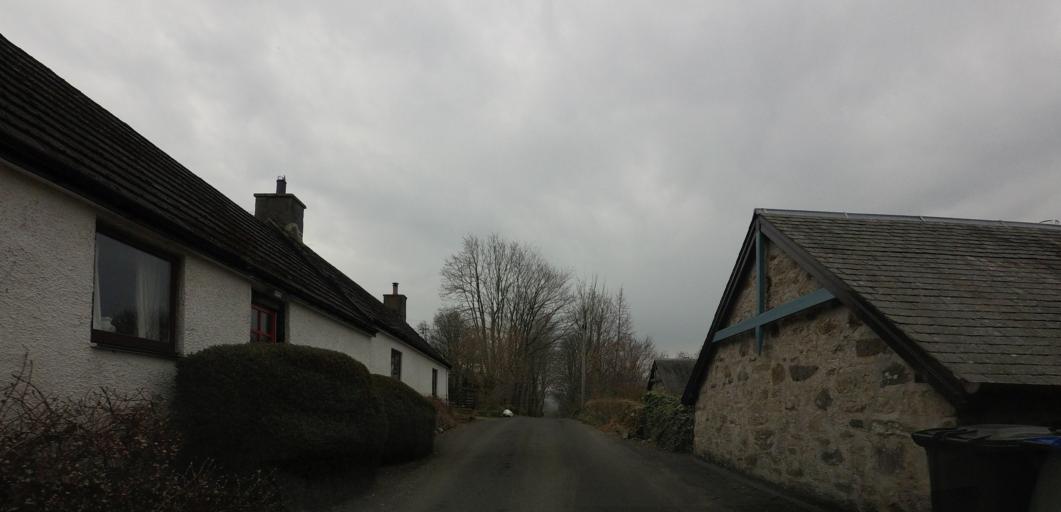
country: GB
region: Scotland
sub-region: Perth and Kinross
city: Comrie
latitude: 56.5372
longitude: -4.1044
